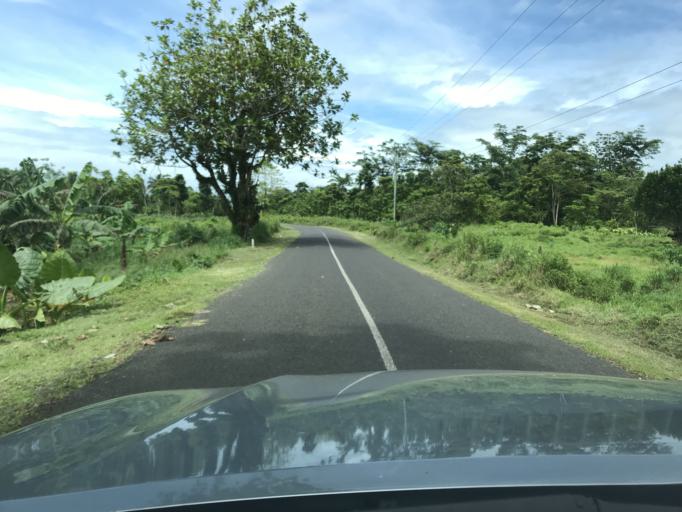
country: WS
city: Fasito`outa
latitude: -13.8640
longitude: -171.9111
